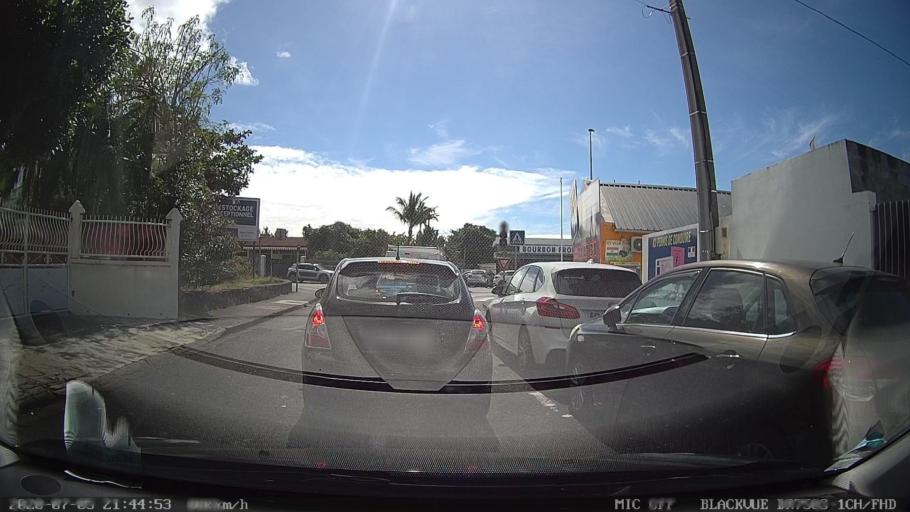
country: RE
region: Reunion
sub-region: Reunion
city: Saint-Denis
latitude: -20.8868
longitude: 55.4794
